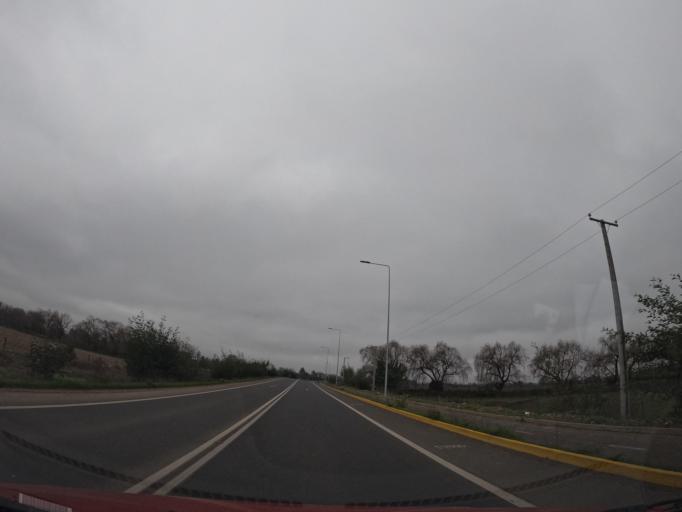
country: CL
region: Maule
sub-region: Provincia de Talca
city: San Clemente
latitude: -35.5099
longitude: -71.5121
